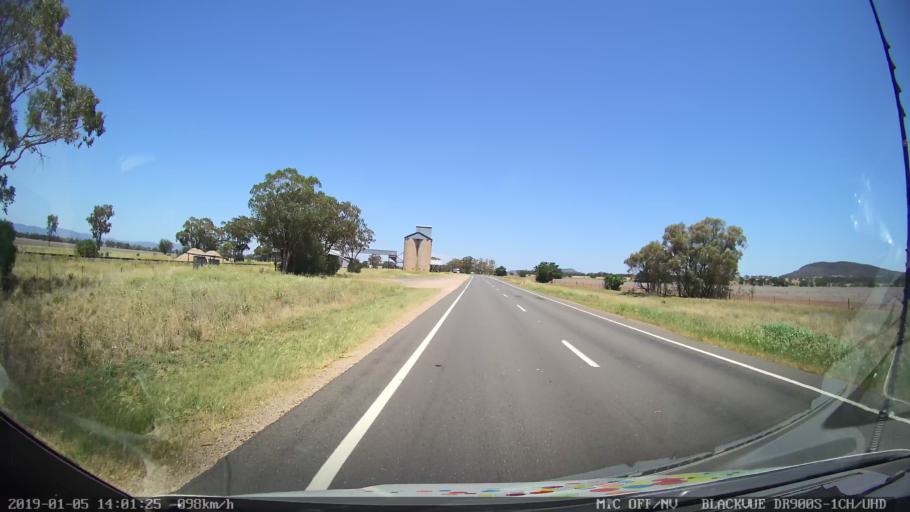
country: AU
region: New South Wales
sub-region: Gunnedah
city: Gunnedah
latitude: -31.1696
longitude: 150.3249
